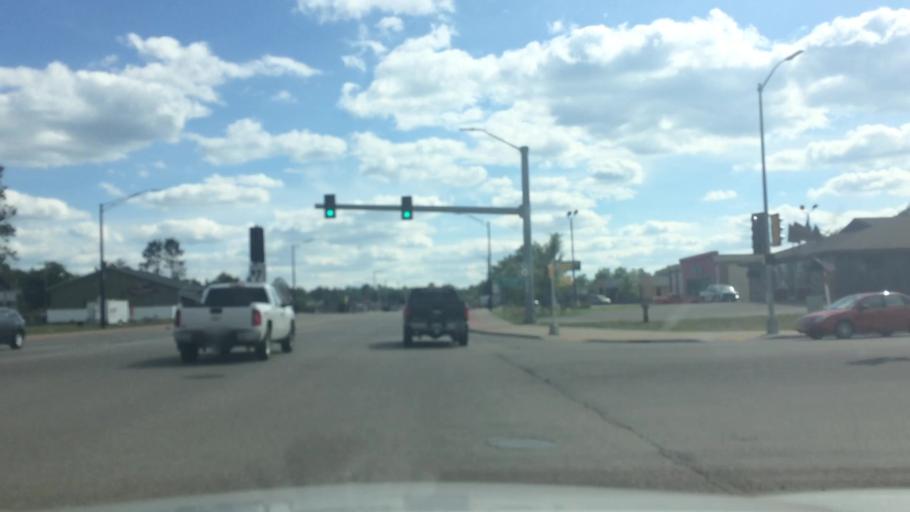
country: US
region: Wisconsin
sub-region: Vilas County
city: Lac du Flambeau
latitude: 45.8909
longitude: -89.7012
